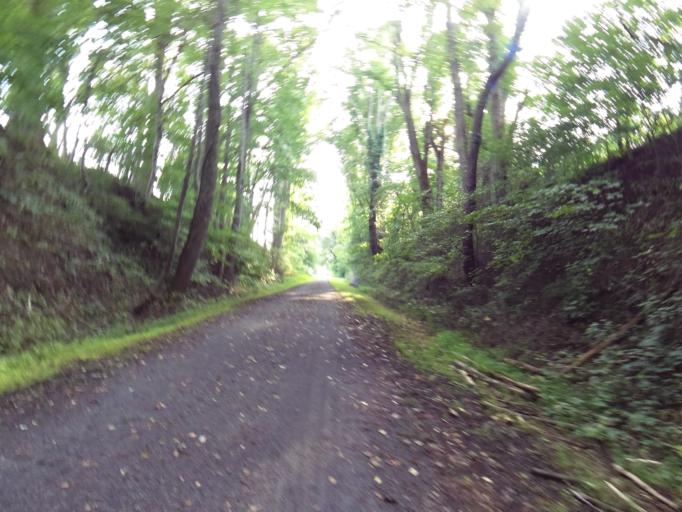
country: US
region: Virginia
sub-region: Washington County
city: Abingdon
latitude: 36.6779
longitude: -81.9317
